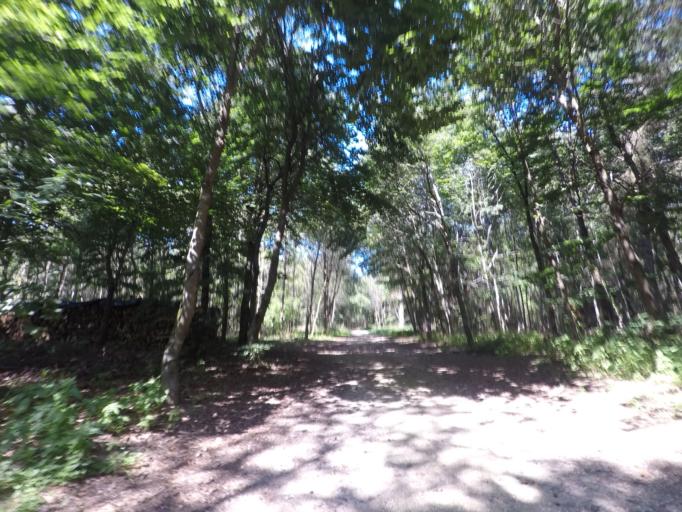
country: LU
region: Luxembourg
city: Bereldange
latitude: 49.6355
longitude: 6.1117
